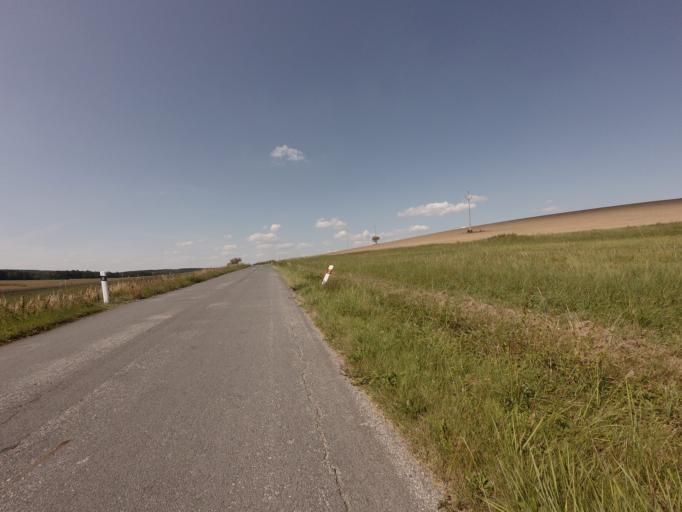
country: CZ
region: Jihocesky
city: Tyn nad Vltavou
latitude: 49.1412
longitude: 14.4477
